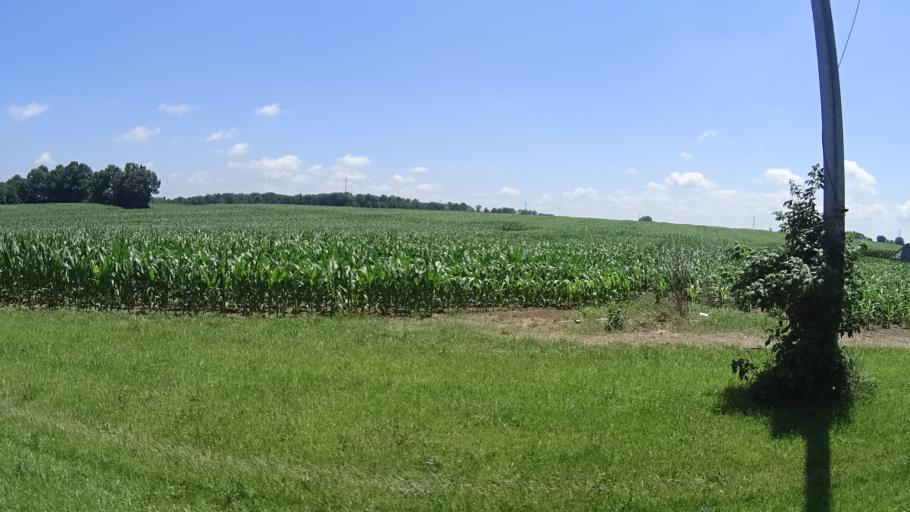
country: US
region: Ohio
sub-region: Lorain County
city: Vermilion
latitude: 41.3471
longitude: -82.4183
